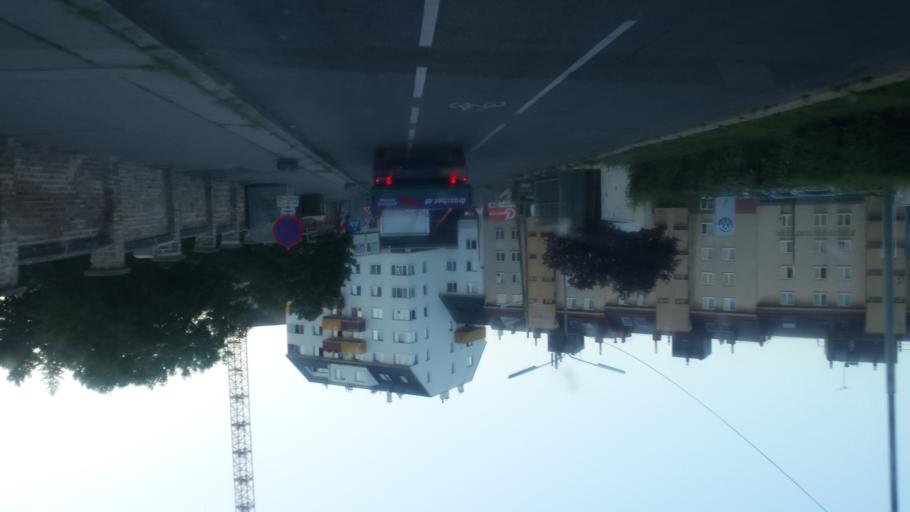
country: AT
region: Lower Austria
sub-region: Politischer Bezirk Wien-Umgebung
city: Schwechat
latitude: 48.1698
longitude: 16.4238
